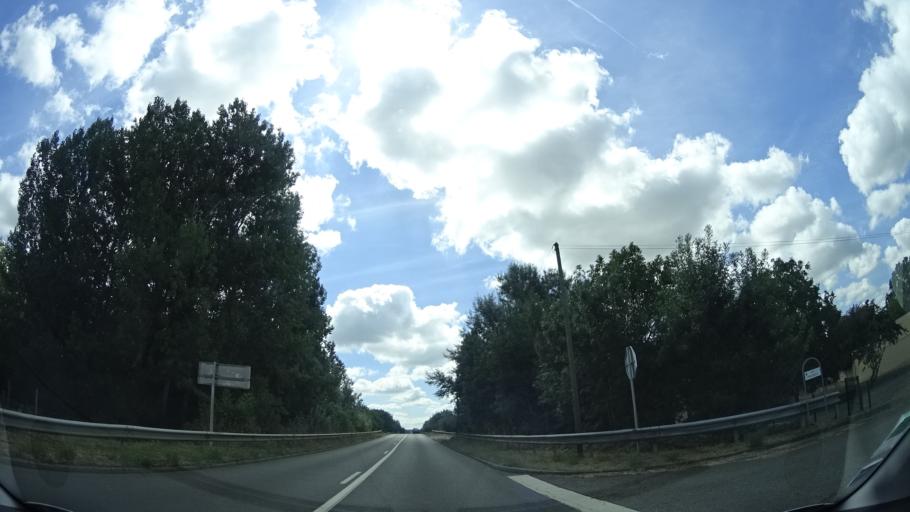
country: FR
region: Pays de la Loire
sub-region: Departement de la Sarthe
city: La Fleche
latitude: 47.6968
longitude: -0.0865
